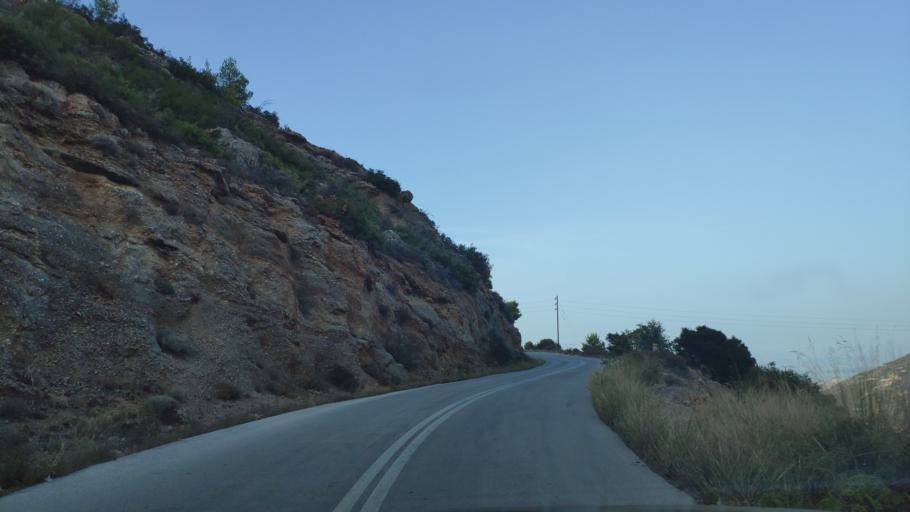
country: GR
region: West Greece
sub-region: Nomos Achaias
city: Aiyira
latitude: 38.0939
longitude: 22.4078
